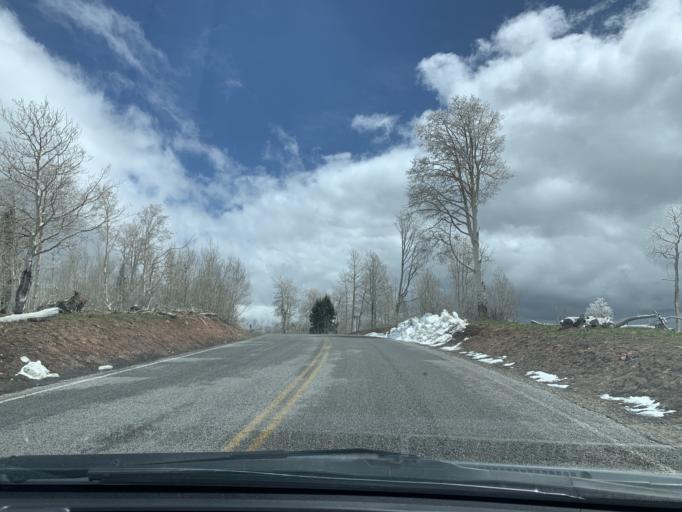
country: US
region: Utah
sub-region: Juab County
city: Mona
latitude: 39.8462
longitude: -111.7139
